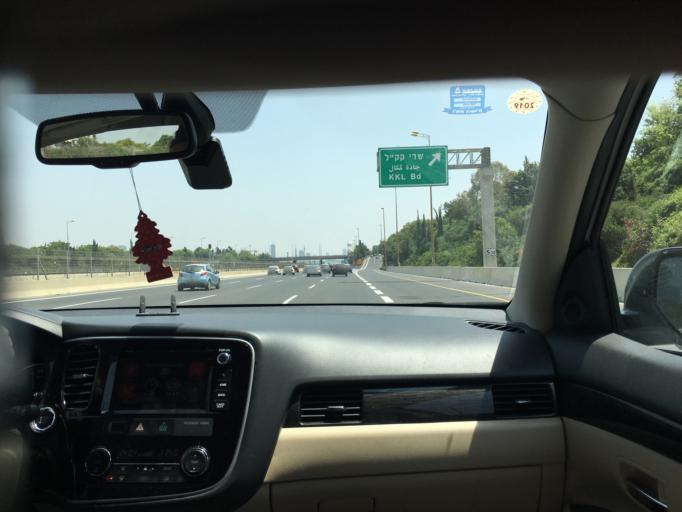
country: IL
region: Tel Aviv
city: Ramat HaSharon
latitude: 32.1236
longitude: 34.8099
